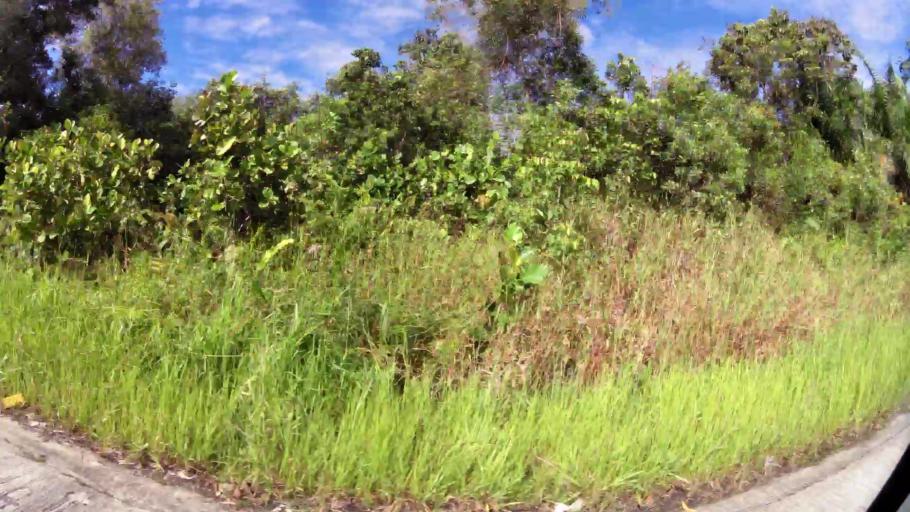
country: BN
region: Brunei and Muara
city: Bandar Seri Begawan
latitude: 4.9022
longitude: 114.9728
